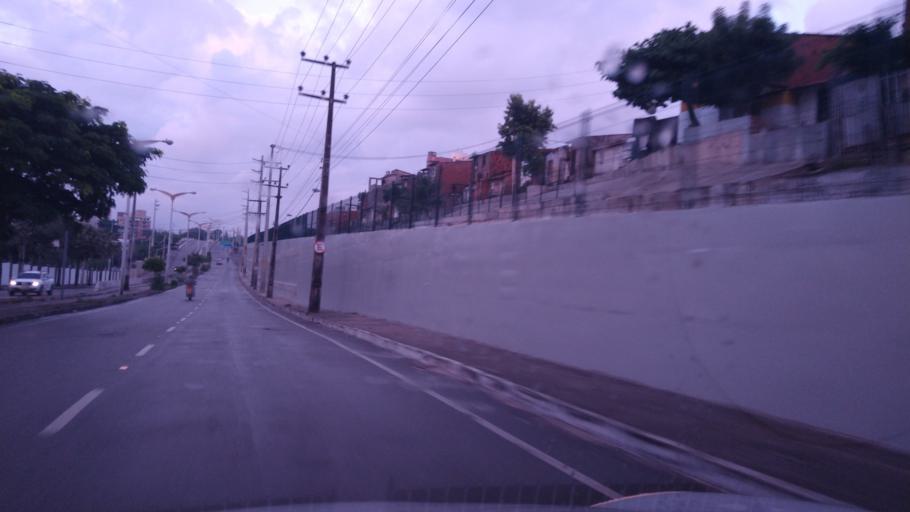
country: BR
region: Ceara
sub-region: Fortaleza
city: Fortaleza
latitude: -3.7457
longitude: -38.4910
